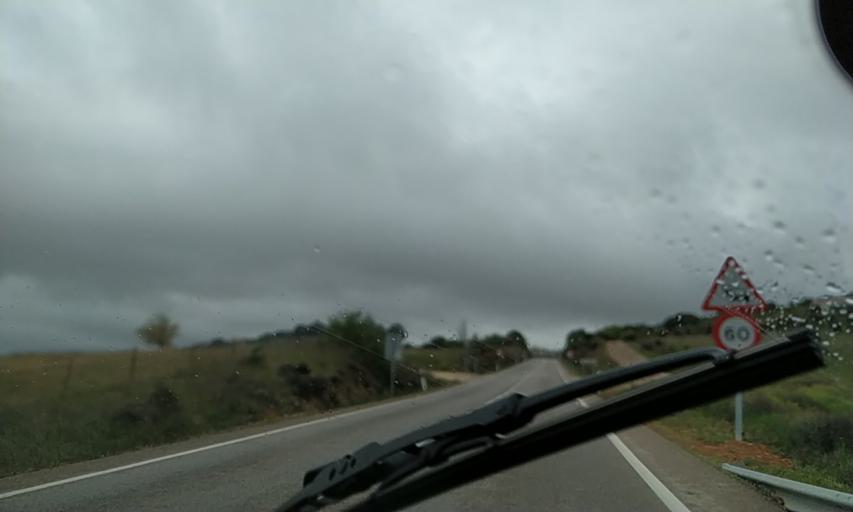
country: ES
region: Extremadura
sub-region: Provincia de Caceres
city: Caceres
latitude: 39.4908
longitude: -6.3842
